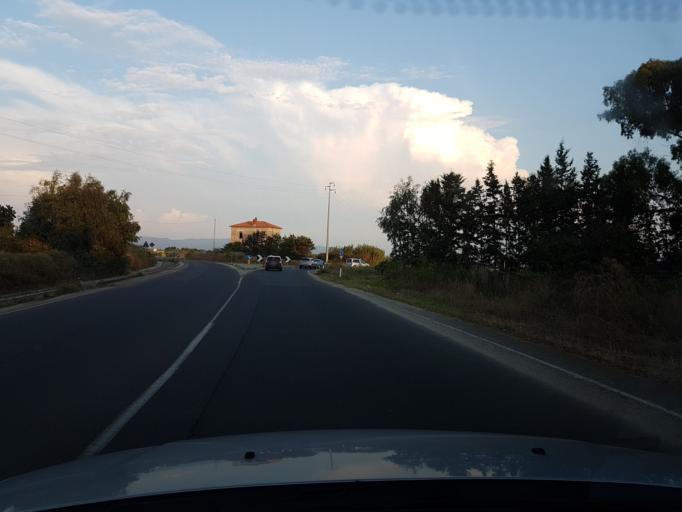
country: IT
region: Sardinia
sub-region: Provincia di Oristano
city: Cabras
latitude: 39.9151
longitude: 8.5413
